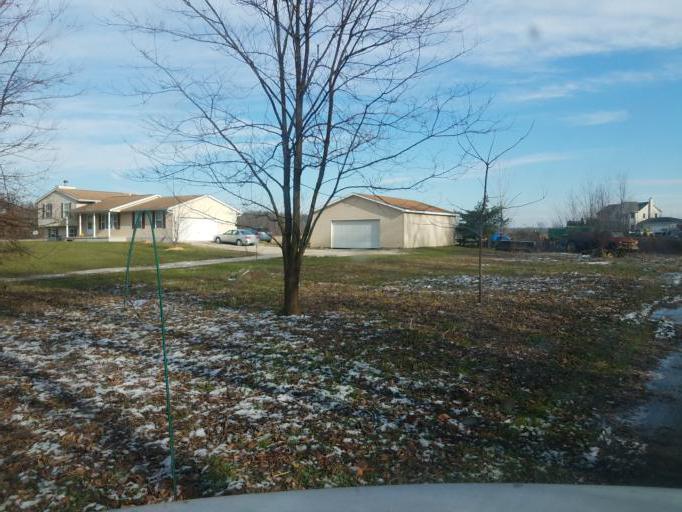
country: US
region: Ohio
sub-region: Delaware County
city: Ashley
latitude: 40.3717
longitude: -82.9284
